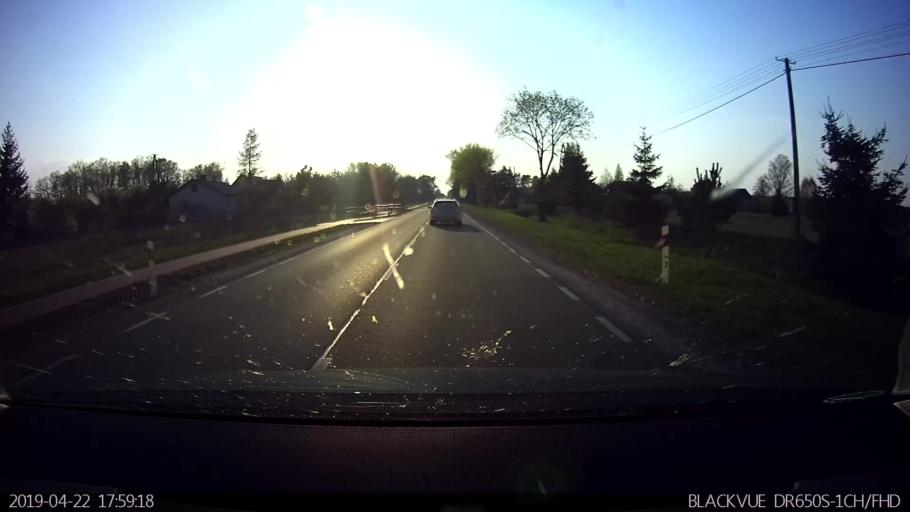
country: PL
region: Masovian Voivodeship
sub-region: Powiat wegrowski
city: Korytnica
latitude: 52.4734
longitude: 21.8656
